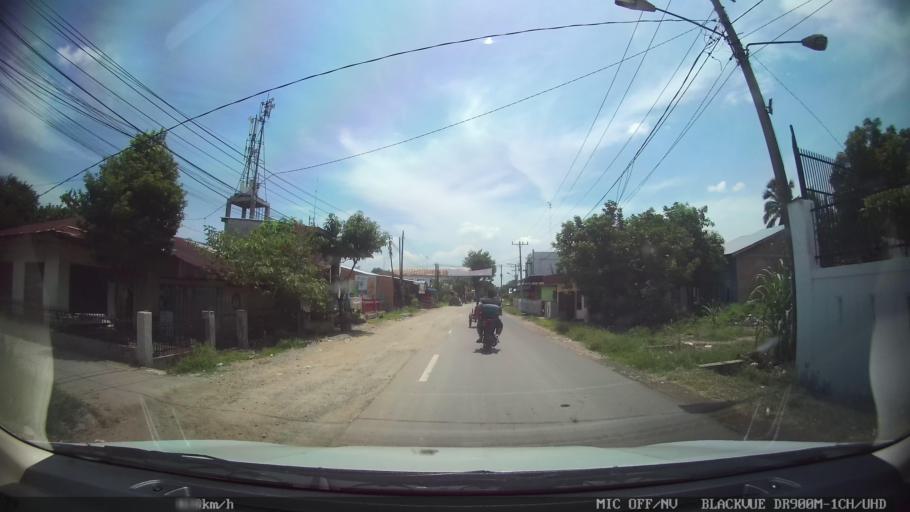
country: ID
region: North Sumatra
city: Binjai
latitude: 3.5941
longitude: 98.4912
